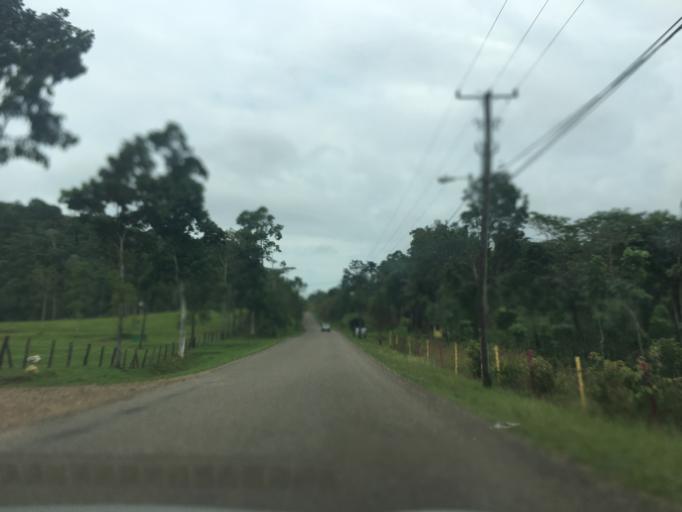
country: BZ
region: Cayo
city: Belmopan
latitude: 17.0752
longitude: -88.5980
